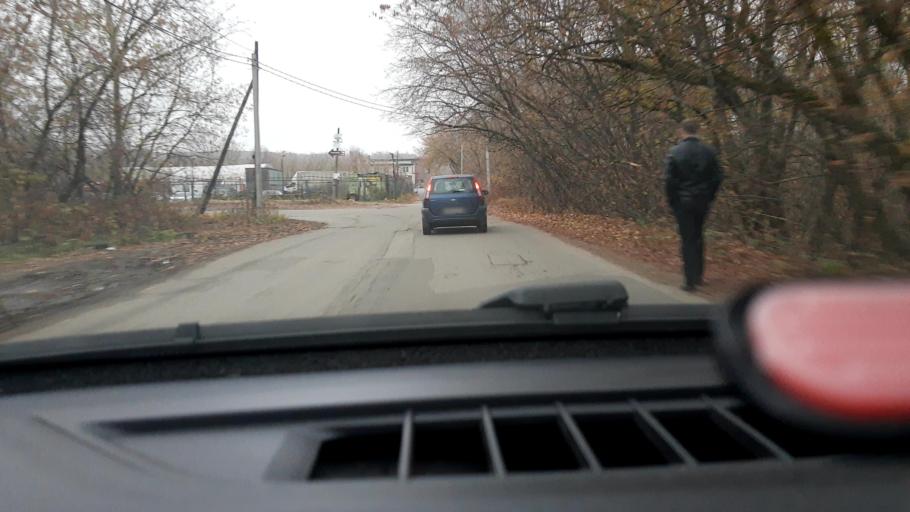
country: RU
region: Nizjnij Novgorod
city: Burevestnik
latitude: 56.2263
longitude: 43.8875
